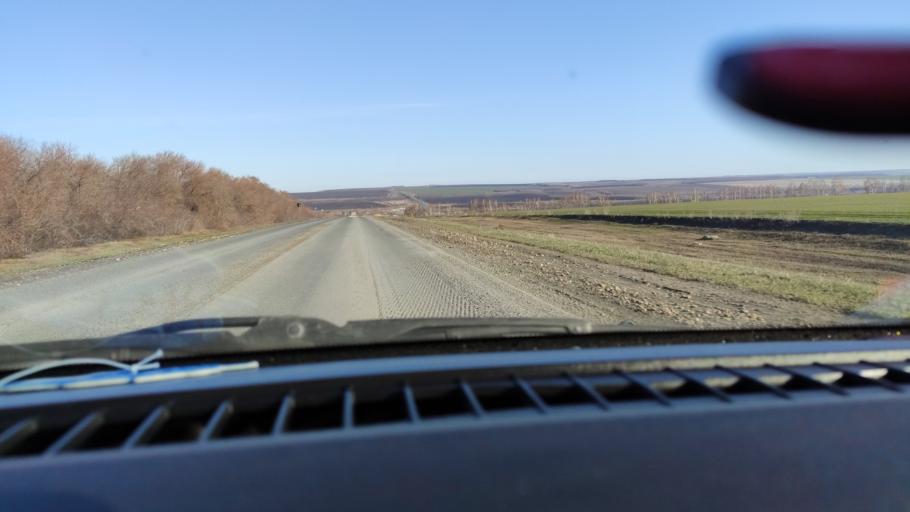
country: RU
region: Saratov
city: Dukhovnitskoye
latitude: 52.7232
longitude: 48.2624
